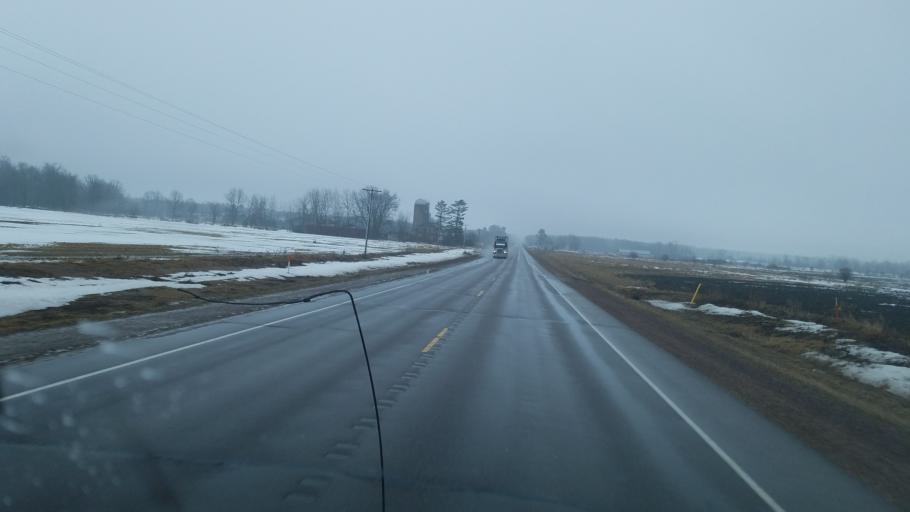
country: US
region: Wisconsin
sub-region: Wood County
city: Marshfield
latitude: 44.5986
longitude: -90.2349
